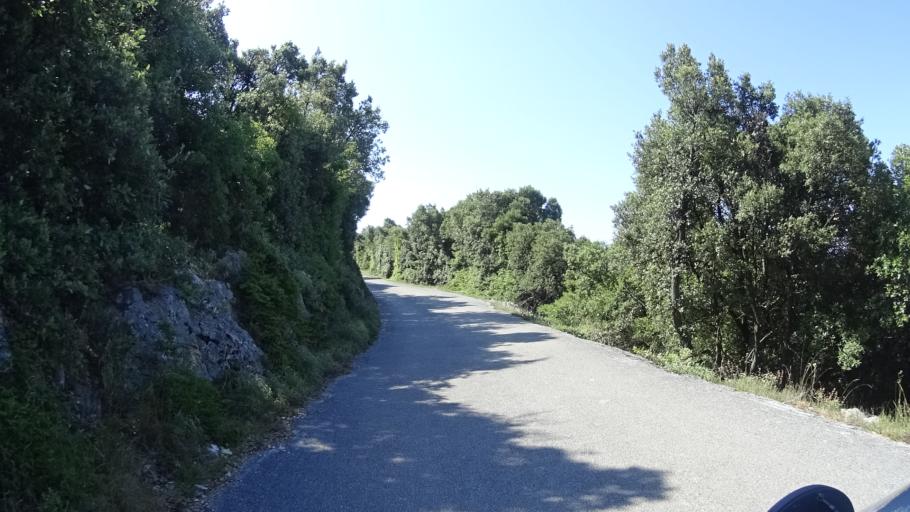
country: HR
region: Istarska
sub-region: Grad Labin
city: Rabac
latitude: 44.9724
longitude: 14.1429
